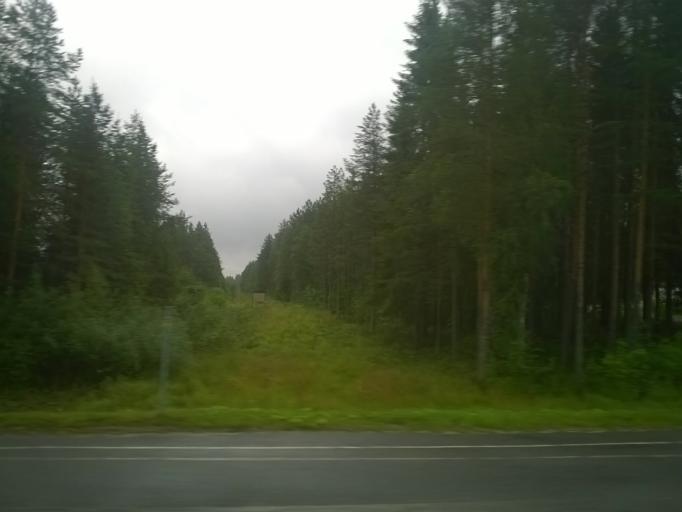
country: FI
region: Kainuu
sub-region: Kehys-Kainuu
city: Kuhmo
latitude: 64.1192
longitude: 29.5019
